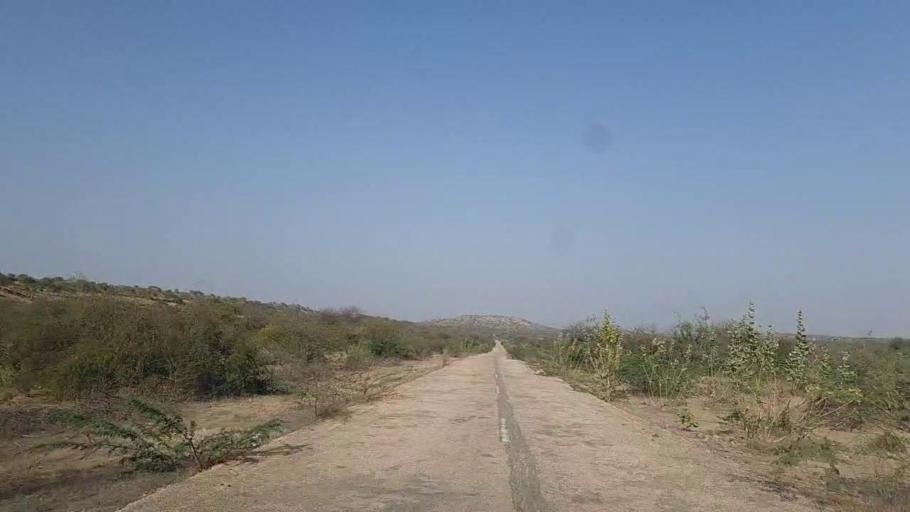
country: PK
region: Sindh
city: Naukot
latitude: 24.6039
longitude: 69.3310
